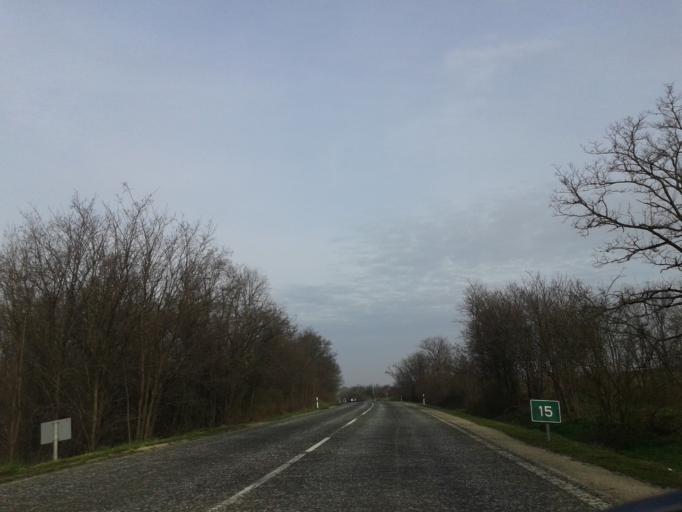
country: HU
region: Pest
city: Biatorbagy
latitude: 47.4847
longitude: 18.8346
